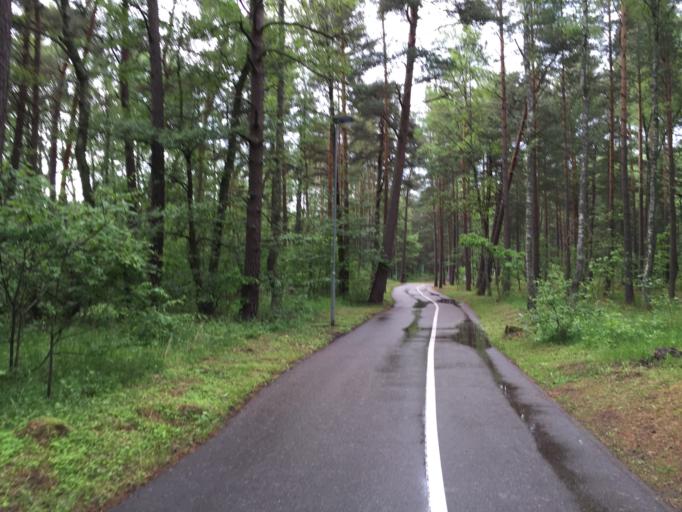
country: LT
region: Klaipedos apskritis
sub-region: Klaipeda
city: Klaipeda
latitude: 55.7511
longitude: 21.1180
